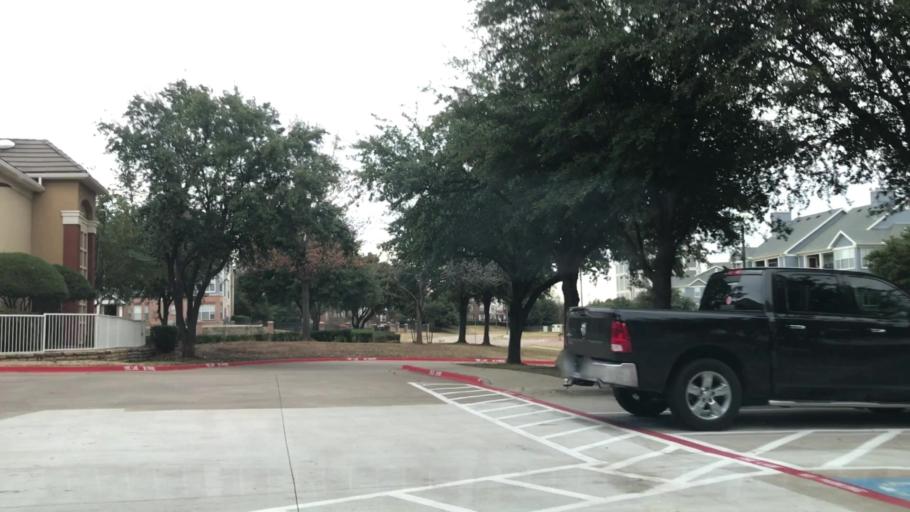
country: US
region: Texas
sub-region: Dallas County
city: Irving
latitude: 32.8816
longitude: -96.9614
